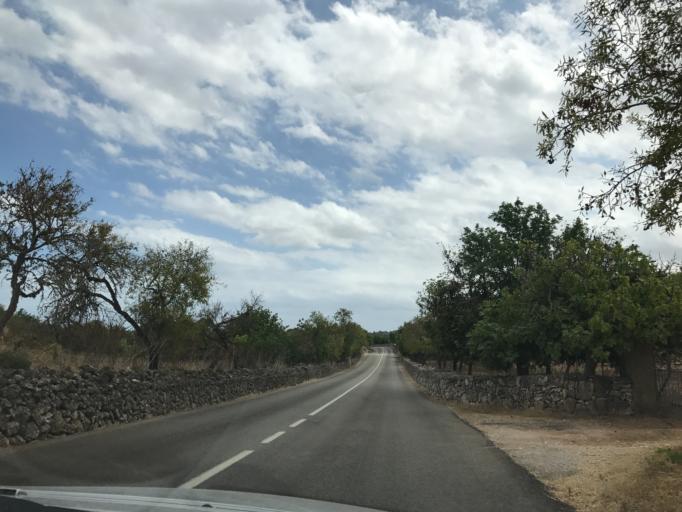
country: ES
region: Balearic Islands
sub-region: Illes Balears
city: Arta
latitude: 39.6667
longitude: 3.3320
